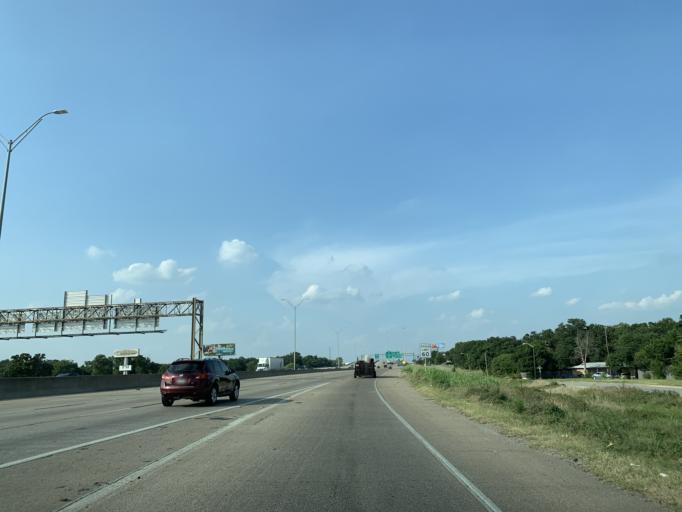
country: US
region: Texas
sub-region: Tarrant County
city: Richland Hills
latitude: 32.7480
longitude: -97.2206
